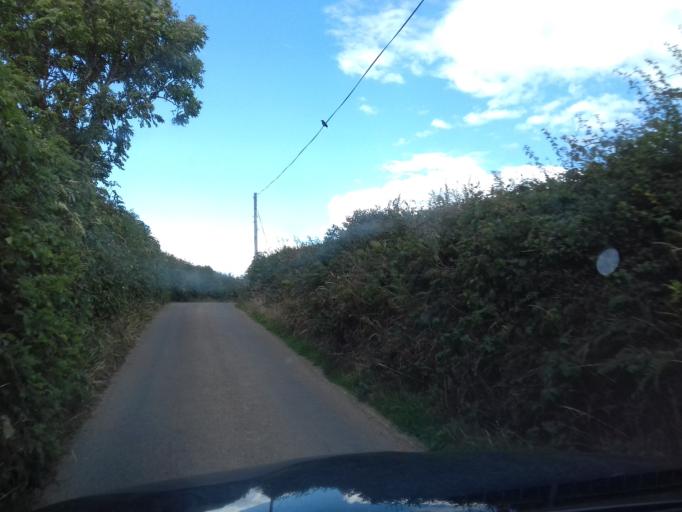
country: IE
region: Leinster
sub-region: Kilkenny
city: Graiguenamanagh
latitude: 52.5823
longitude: -7.0056
